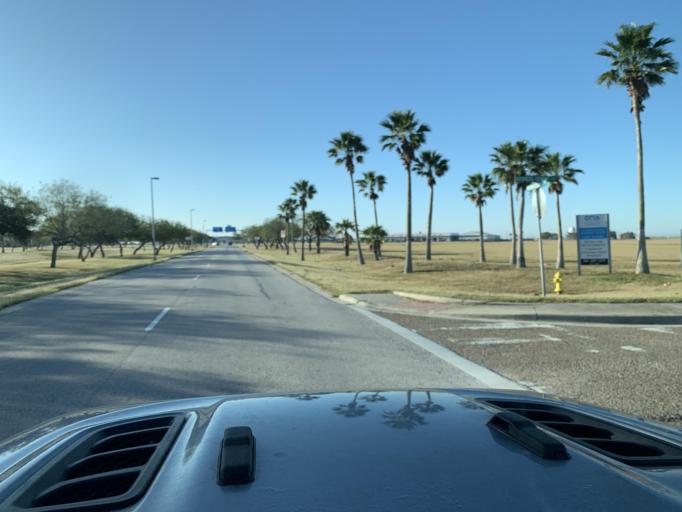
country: US
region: Texas
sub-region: Nueces County
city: Corpus Christi
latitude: 27.7826
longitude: -97.5024
